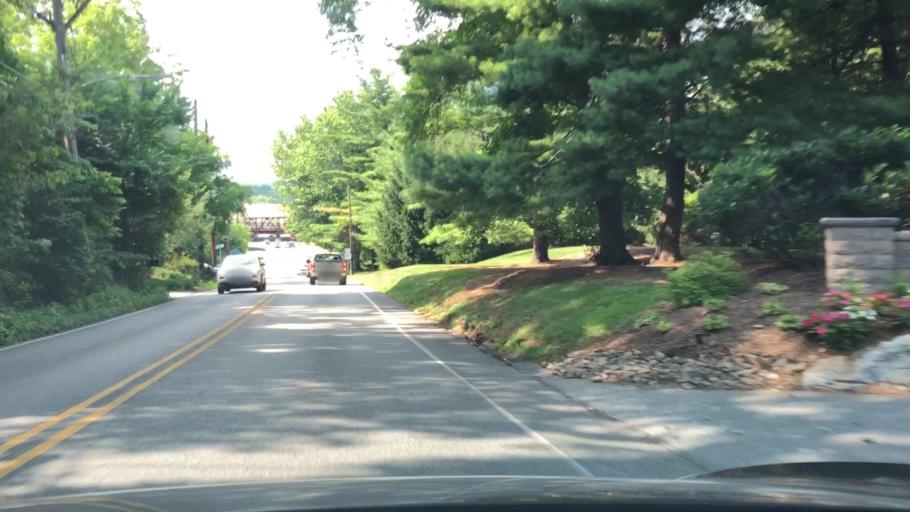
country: US
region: Pennsylvania
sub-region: Chester County
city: Devon
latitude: 40.0692
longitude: -75.4353
